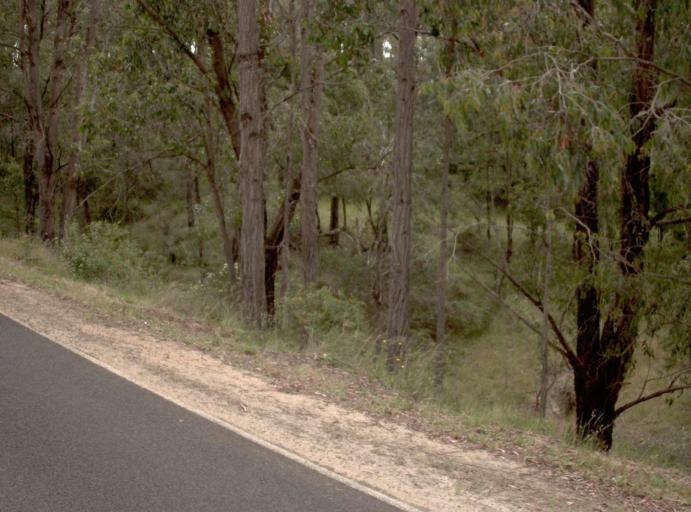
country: AU
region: Victoria
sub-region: Latrobe
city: Traralgon
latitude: -38.4114
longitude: 146.8190
